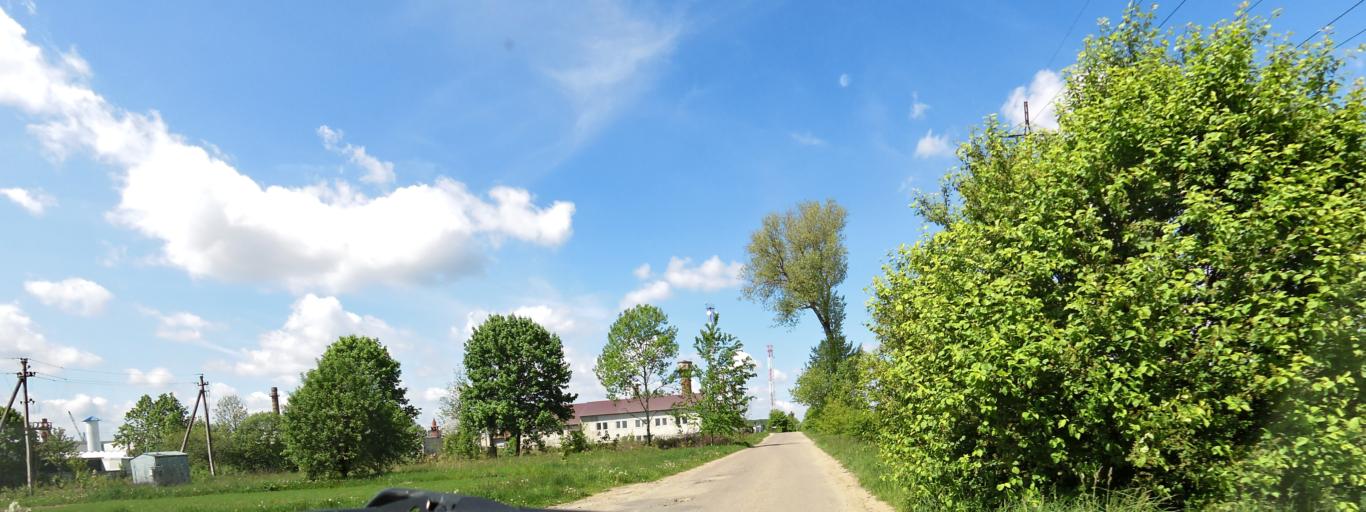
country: LT
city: Lentvaris
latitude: 54.6411
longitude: 25.0629
